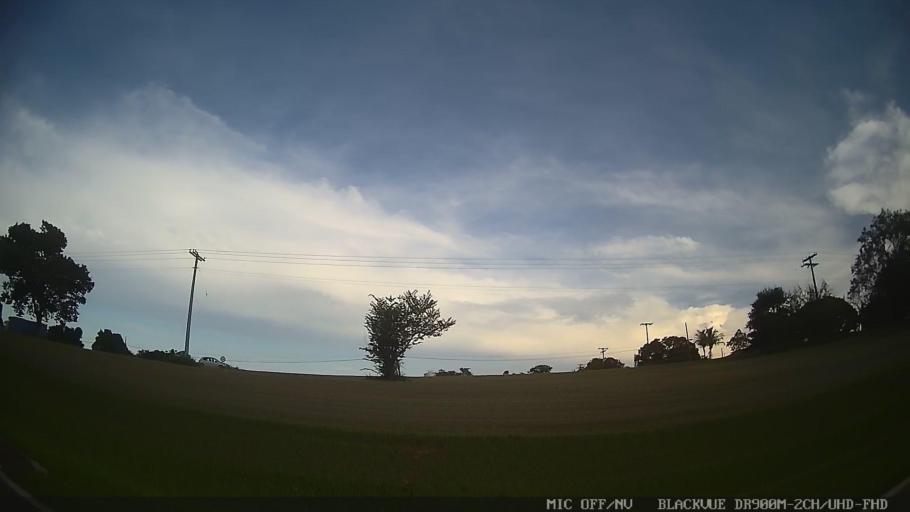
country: BR
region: Sao Paulo
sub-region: Tiete
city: Tiete
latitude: -23.0592
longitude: -47.7235
